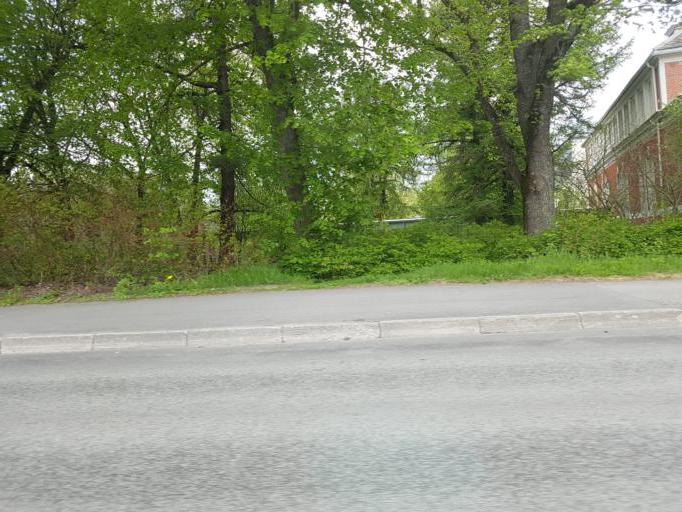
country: NO
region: Nord-Trondelag
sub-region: Levanger
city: Levanger
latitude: 63.7424
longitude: 11.2869
